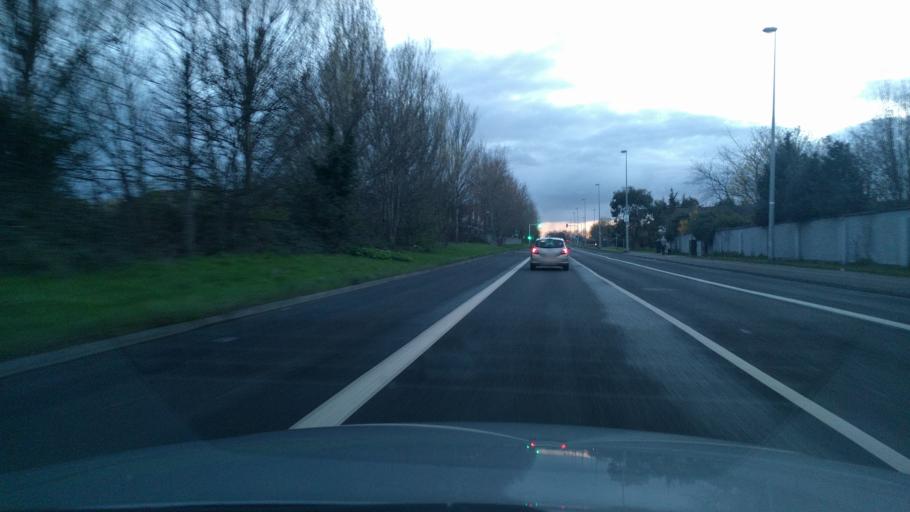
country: IE
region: Leinster
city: Clondalkin
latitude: 53.3263
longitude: -6.4002
